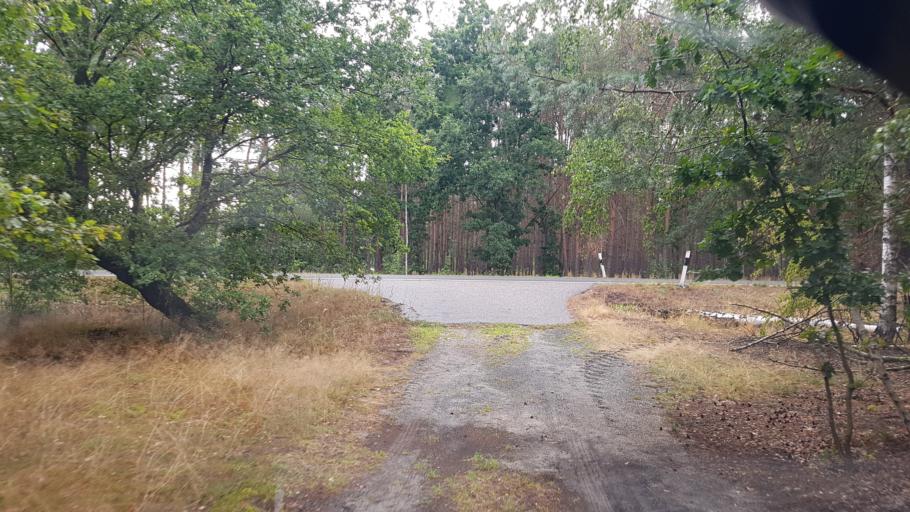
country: DE
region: Brandenburg
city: Schilda
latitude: 51.6259
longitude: 13.3675
